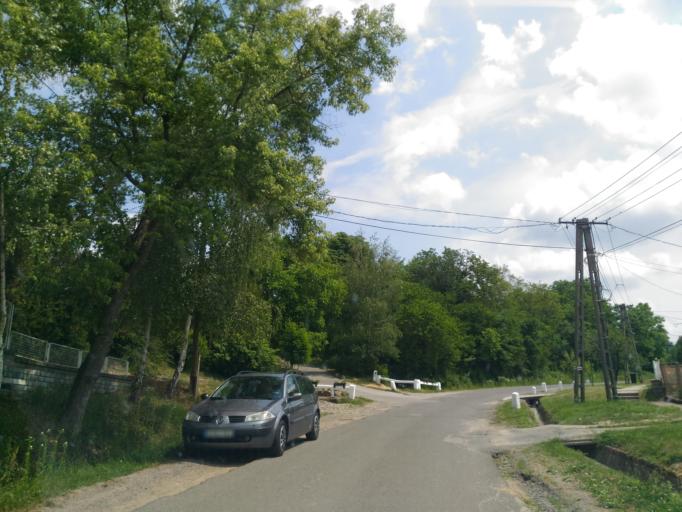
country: HU
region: Baranya
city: Komlo
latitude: 46.1951
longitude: 18.2304
